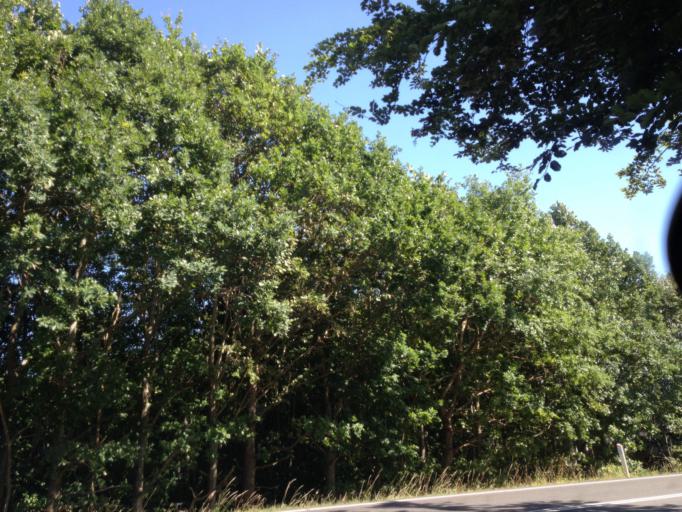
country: DK
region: Capital Region
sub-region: Gribskov Kommune
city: Graested
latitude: 56.0604
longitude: 12.3420
